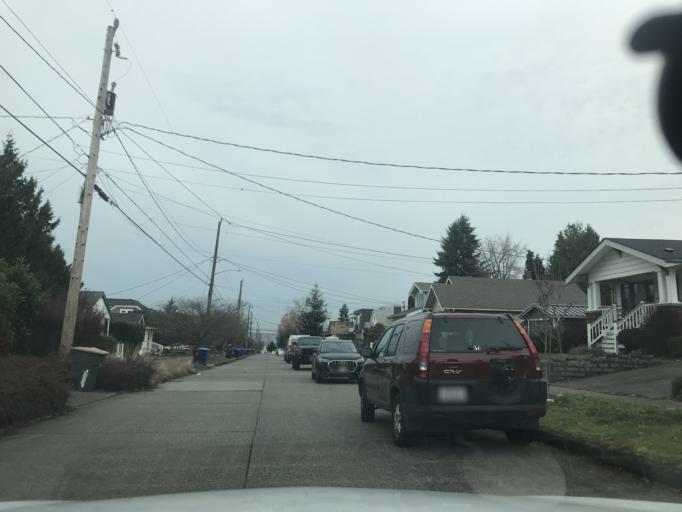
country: US
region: Washington
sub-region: King County
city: Seattle
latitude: 47.5669
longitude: -122.3591
